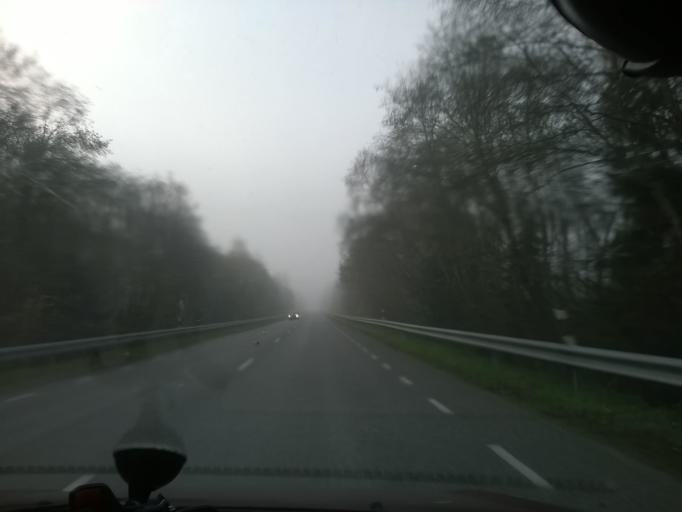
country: EE
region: Tartu
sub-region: Noo vald
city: Noo
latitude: 58.1485
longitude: 26.5253
